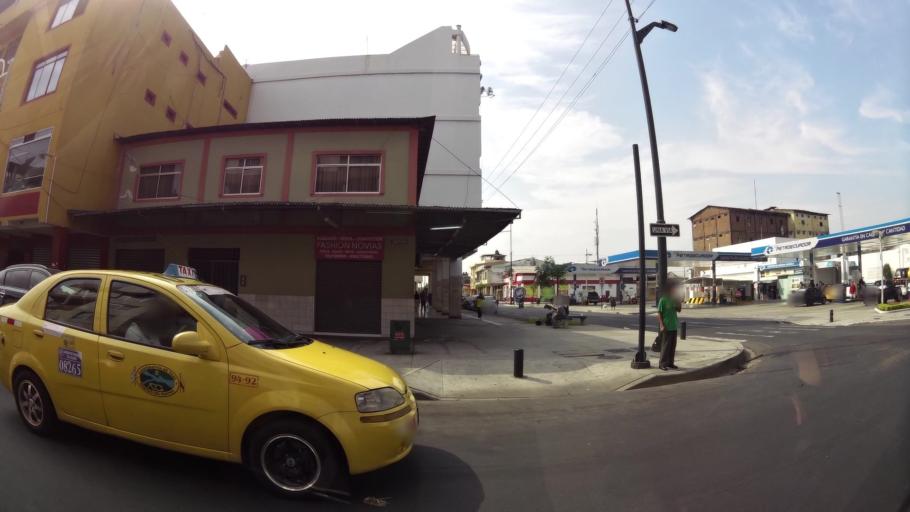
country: EC
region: Guayas
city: Guayaquil
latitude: -2.2005
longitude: -79.9004
